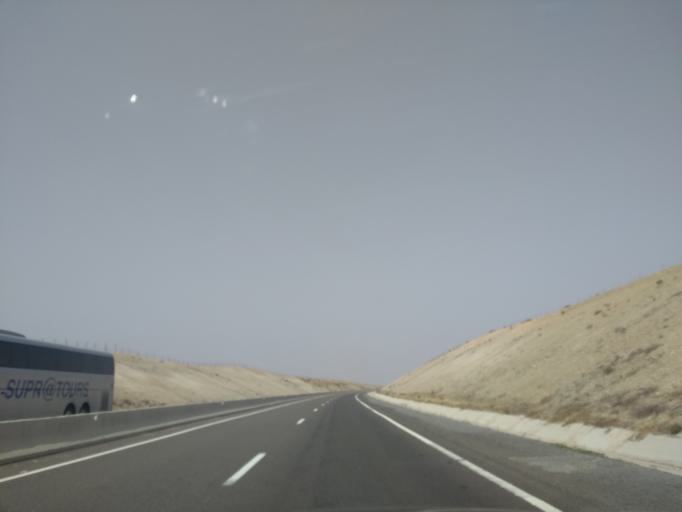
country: MA
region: Marrakech-Tensift-Al Haouz
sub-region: Chichaoua
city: Chichaoua
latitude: 31.5116
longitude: -8.5593
